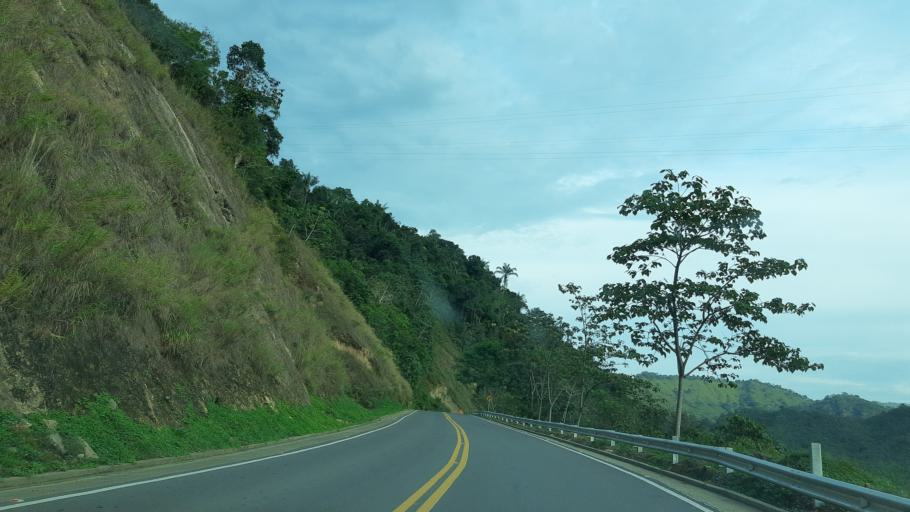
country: CO
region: Boyaca
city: San Luis de Gaceno
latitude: 4.8314
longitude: -73.1525
